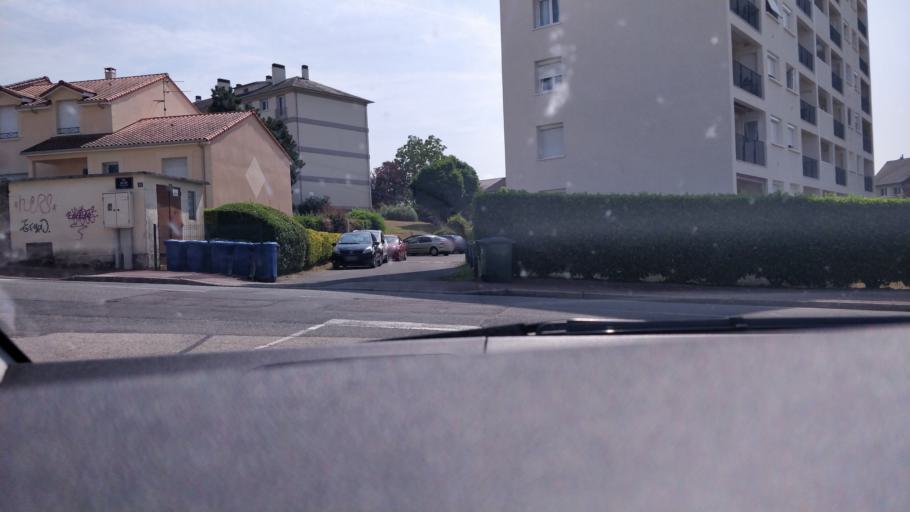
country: FR
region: Limousin
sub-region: Departement de la Haute-Vienne
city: Limoges
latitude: 45.8419
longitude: 1.2411
